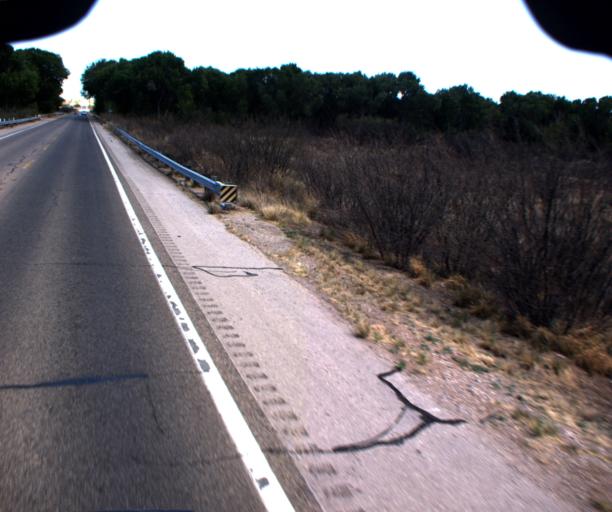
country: US
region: Arizona
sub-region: Cochise County
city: Sierra Vista Southeast
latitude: 31.3799
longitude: -110.1128
